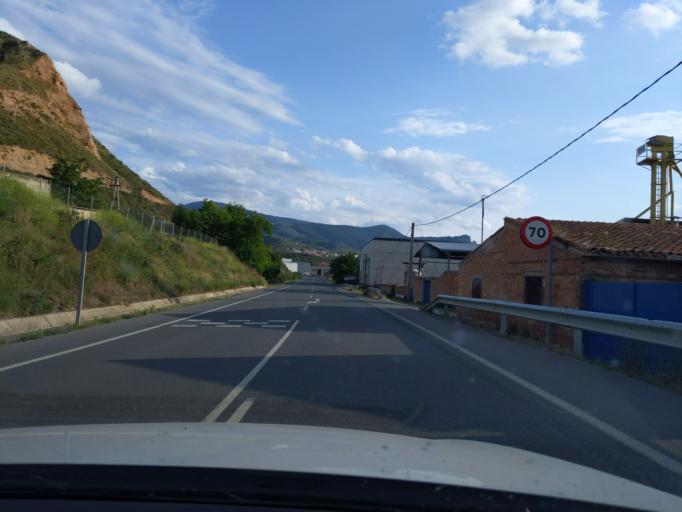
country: ES
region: La Rioja
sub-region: Provincia de La Rioja
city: Albelda de Iregua
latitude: 42.3520
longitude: -2.4768
